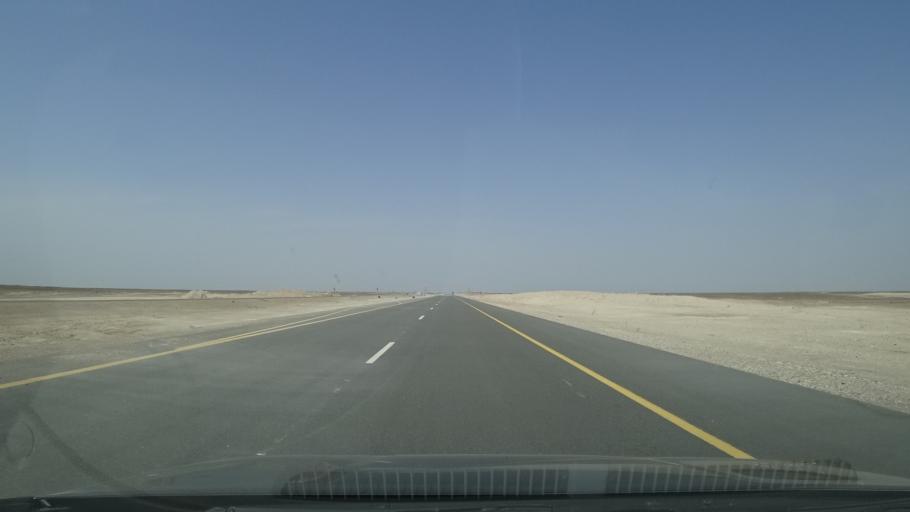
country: OM
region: Muhafazat ad Dakhiliyah
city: Adam
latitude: 21.8417
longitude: 57.3934
